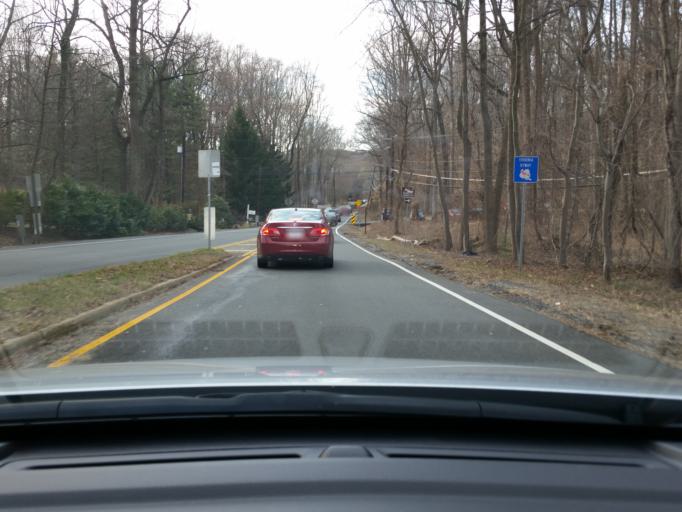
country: US
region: Virginia
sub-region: Fairfax County
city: McLean
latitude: 38.9558
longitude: -77.1973
